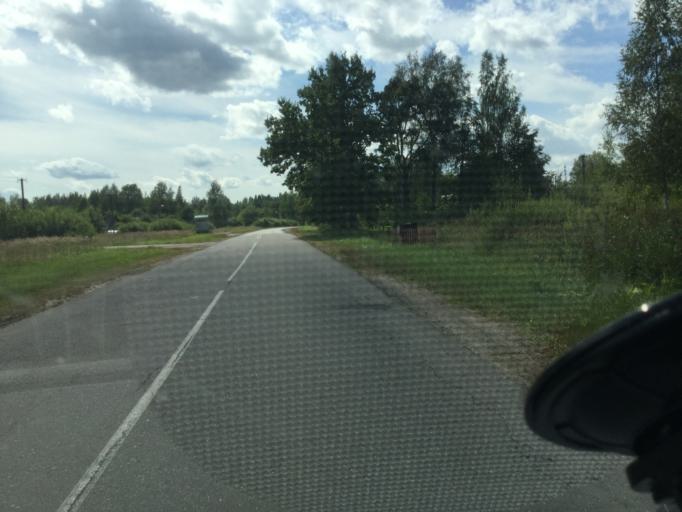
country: BY
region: Vitebsk
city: Chashniki
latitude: 55.2884
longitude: 29.3628
